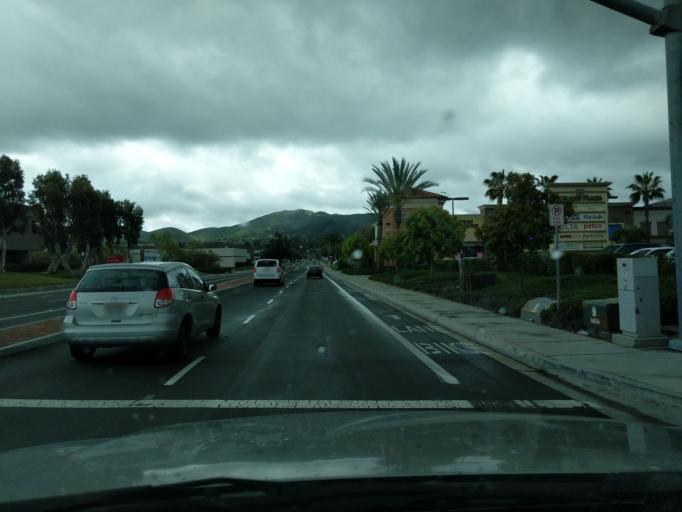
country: US
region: California
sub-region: San Diego County
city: Lake San Marcos
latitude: 33.1401
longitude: -117.1901
